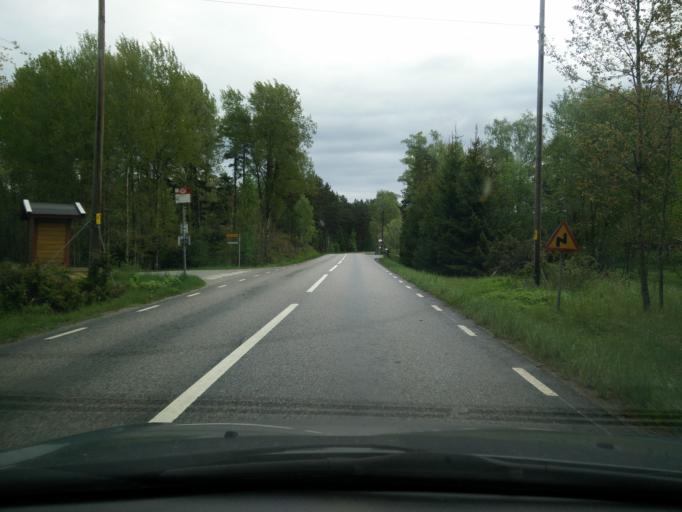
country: SE
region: Stockholm
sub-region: Norrtalje Kommun
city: Bjorko
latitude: 59.8032
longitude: 18.8765
